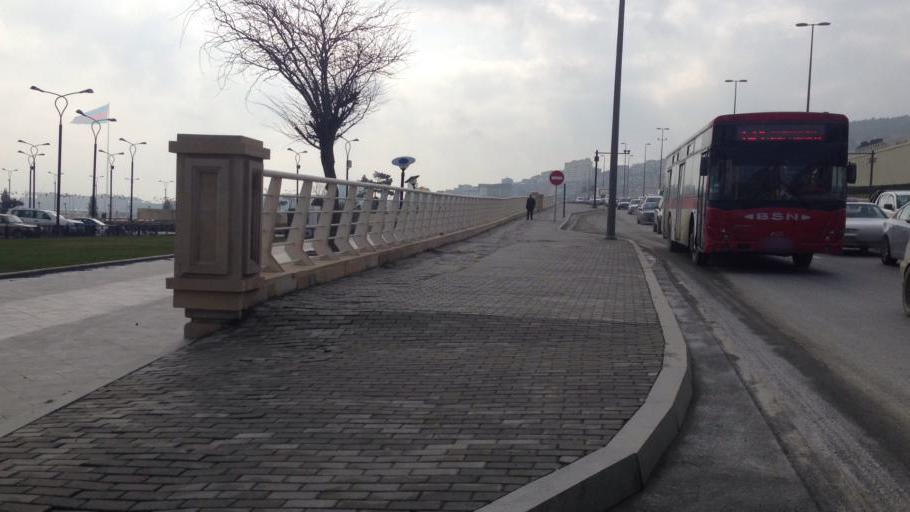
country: AZ
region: Baki
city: Badamdar
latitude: 40.3574
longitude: 49.8343
